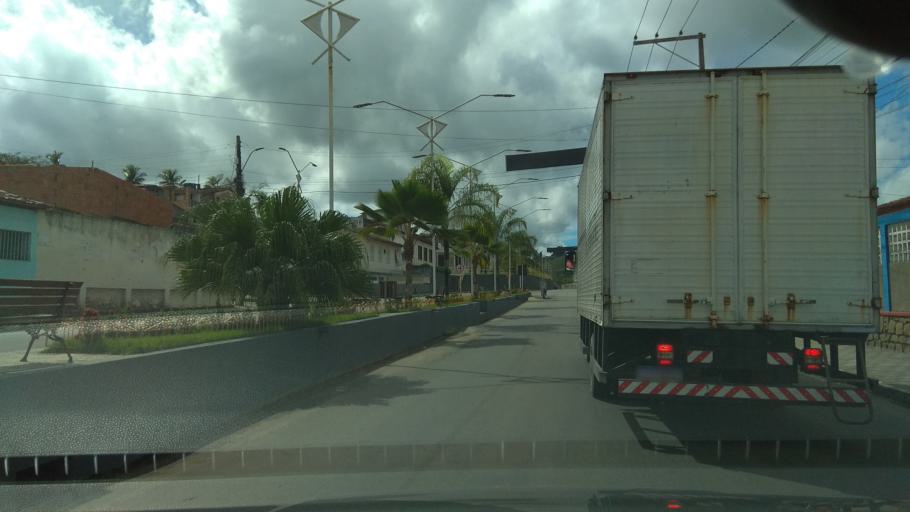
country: BR
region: Bahia
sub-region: Mutuipe
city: Mutuipe
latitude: -13.1805
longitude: -39.4180
